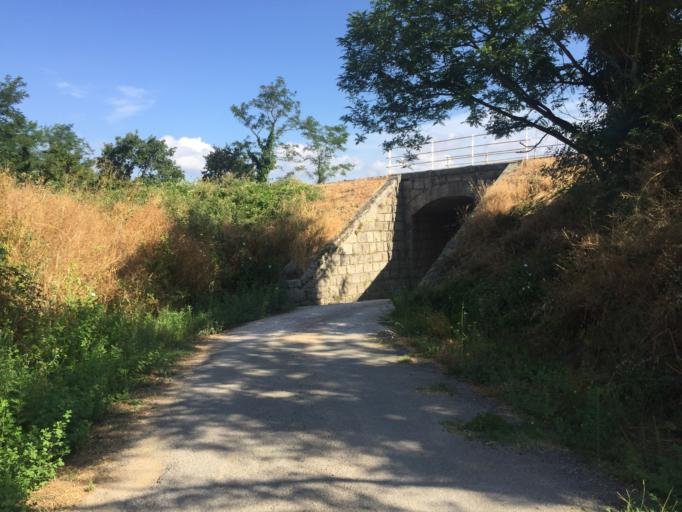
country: IT
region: Sardinia
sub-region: Provincia di Olbia-Tempio
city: Tempio Pausania
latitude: 40.9078
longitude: 9.0905
